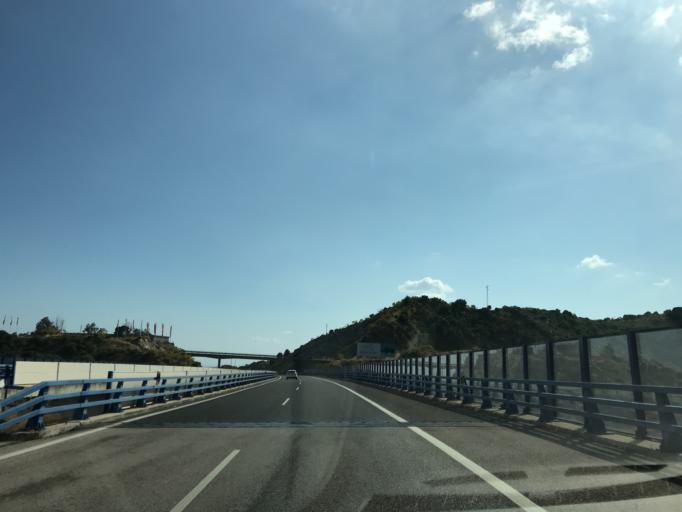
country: ES
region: Andalusia
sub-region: Provincia de Malaga
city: Istan
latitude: 36.5237
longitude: -4.9770
